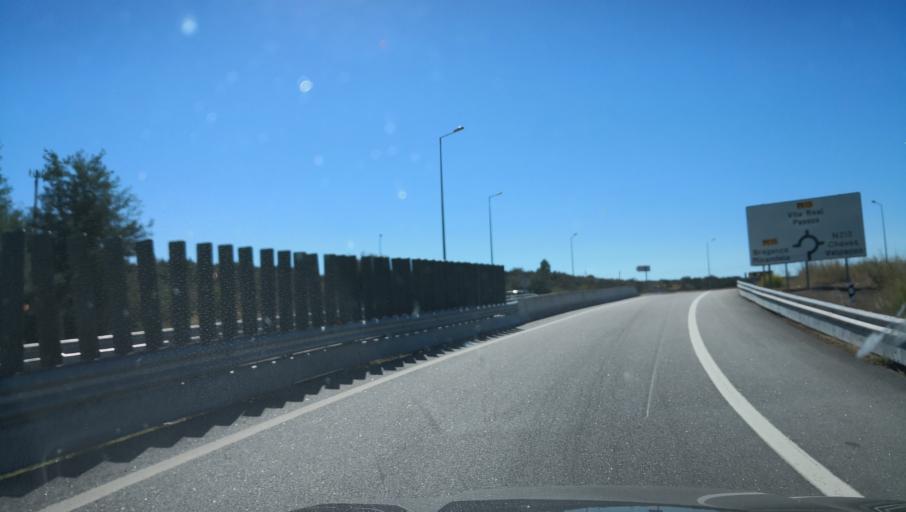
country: PT
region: Braganca
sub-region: Mirandela
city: Mirandela
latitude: 41.4767
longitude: -7.2196
